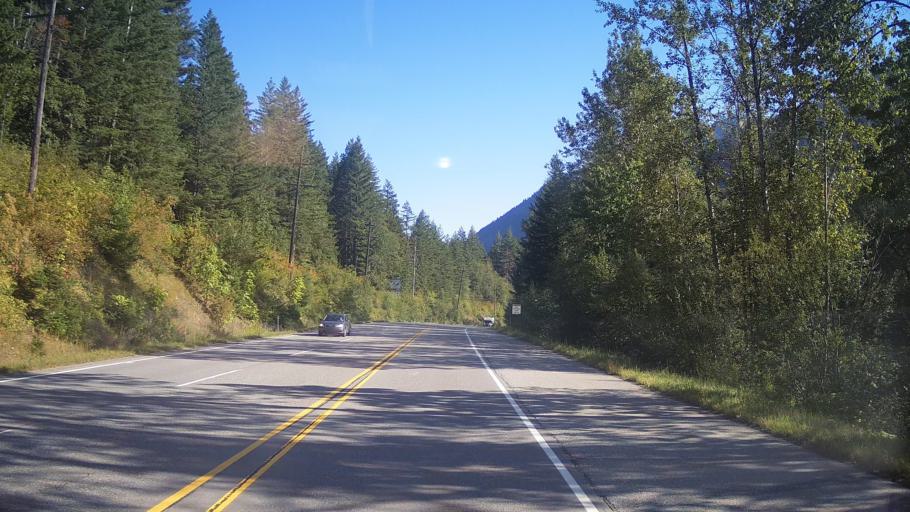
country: CA
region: British Columbia
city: Hope
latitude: 49.5028
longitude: -121.4196
